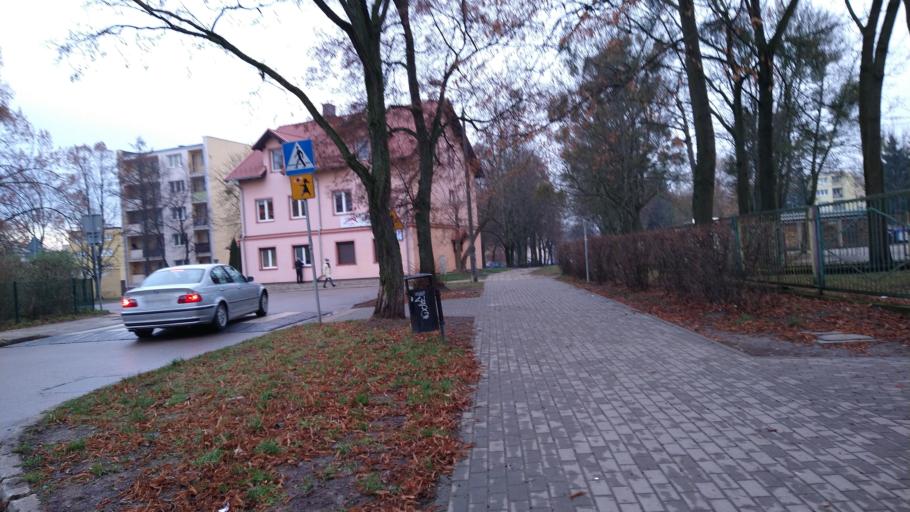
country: PL
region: Warmian-Masurian Voivodeship
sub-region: Powiat olsztynski
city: Olsztyn
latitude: 53.7914
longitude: 20.4982
